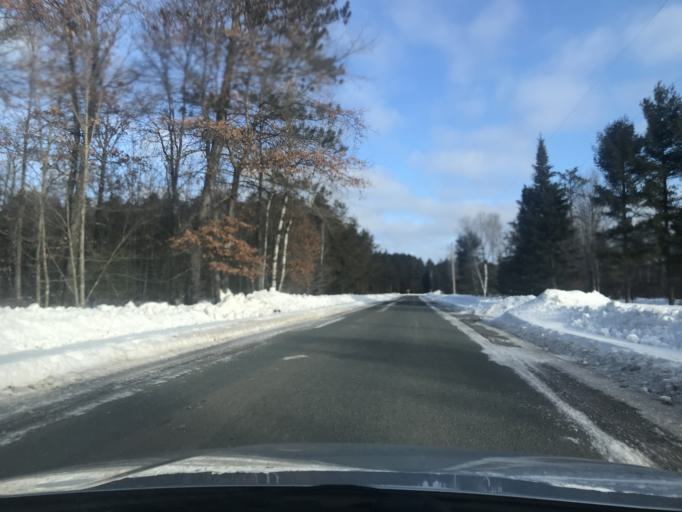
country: US
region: Wisconsin
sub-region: Marinette County
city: Niagara
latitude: 45.6237
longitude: -87.9769
